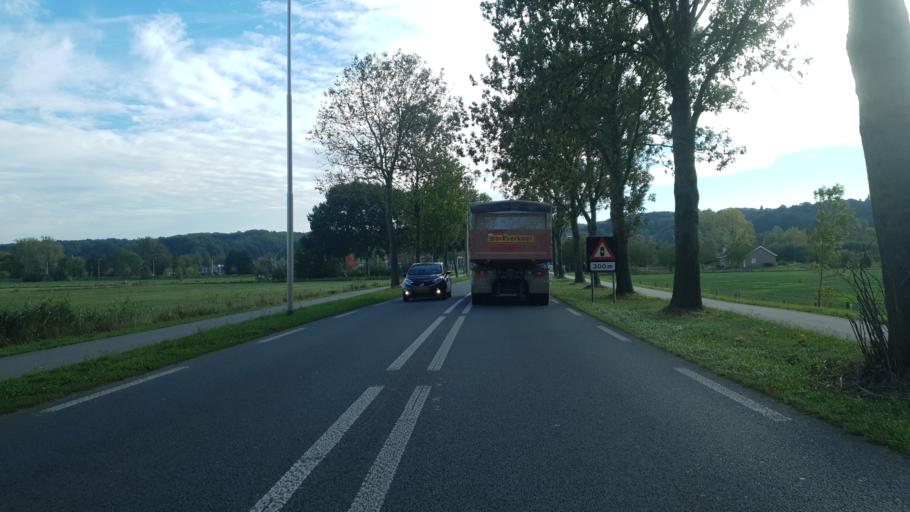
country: NL
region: Gelderland
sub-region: Gemeente Groesbeek
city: Berg en Dal
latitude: 51.8363
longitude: 5.9266
